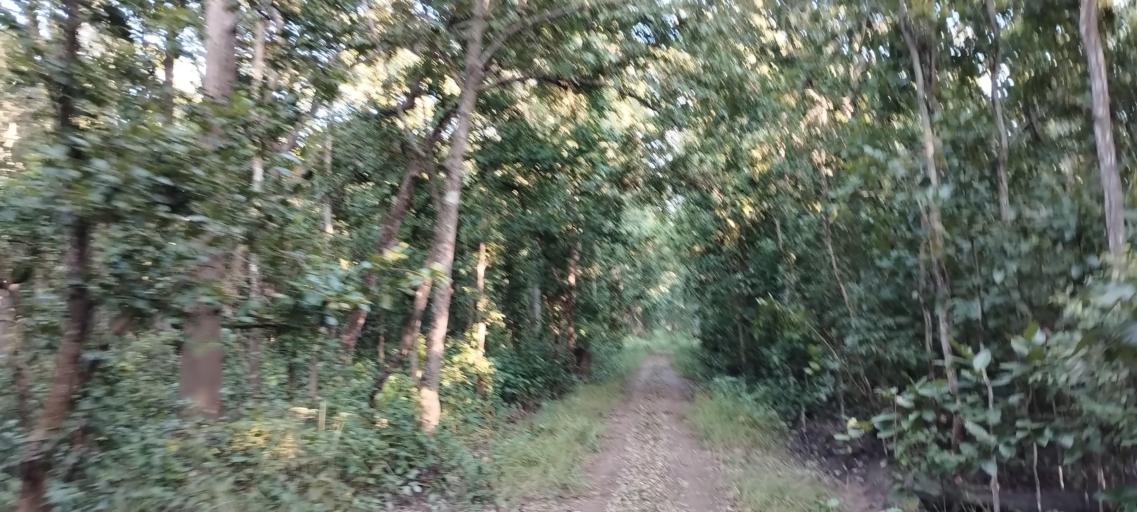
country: NP
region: Far Western
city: Tikapur
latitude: 28.4866
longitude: 81.2622
